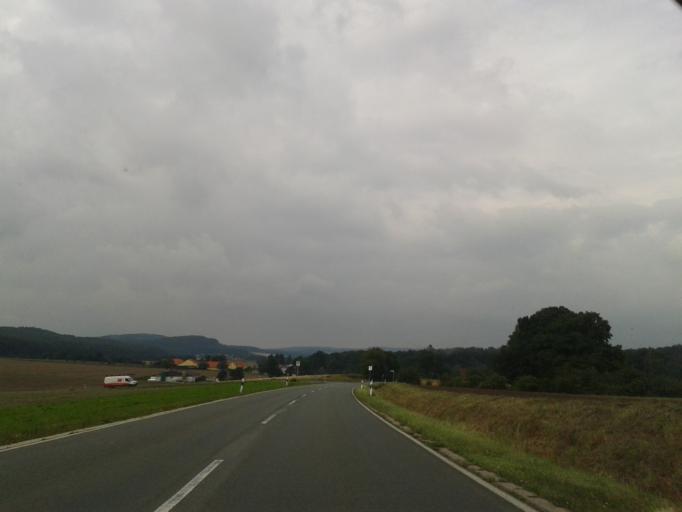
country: DE
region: North Rhine-Westphalia
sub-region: Regierungsbezirk Detmold
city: Barntrup
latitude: 51.9753
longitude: 9.1718
